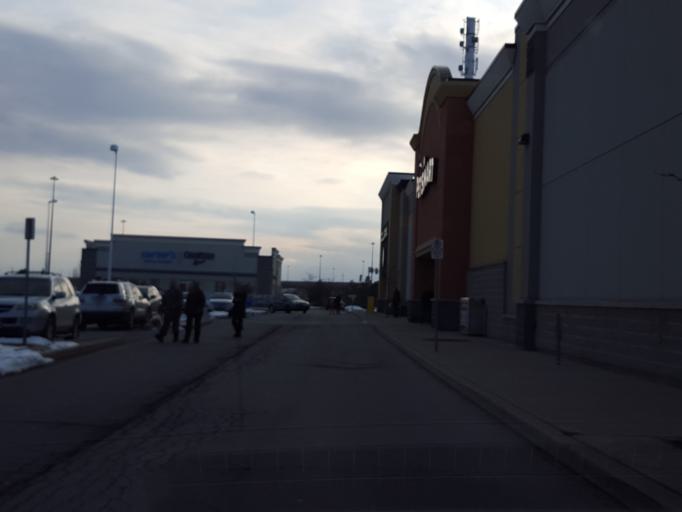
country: CA
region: Ontario
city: Burlington
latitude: 43.3415
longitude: -79.8259
